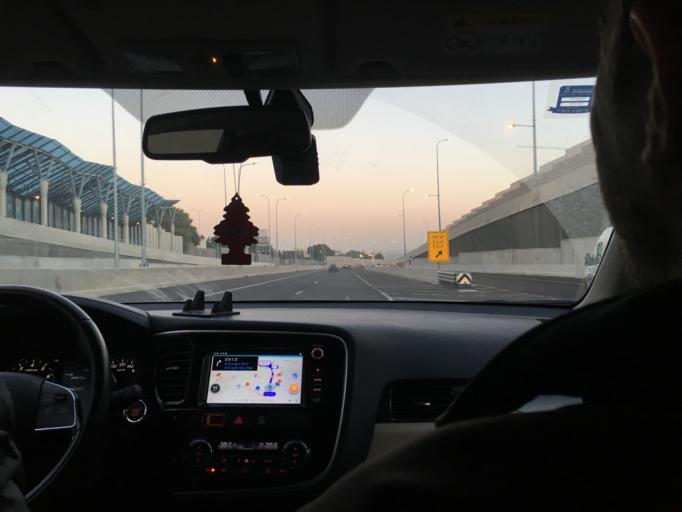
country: IL
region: Central District
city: Hod HaSharon
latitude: 32.1720
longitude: 34.8943
